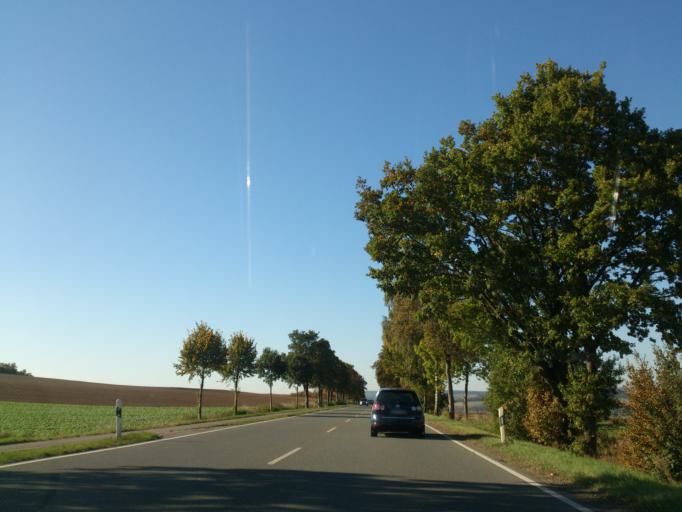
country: DE
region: North Rhine-Westphalia
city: Warburg
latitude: 51.5046
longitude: 9.1020
